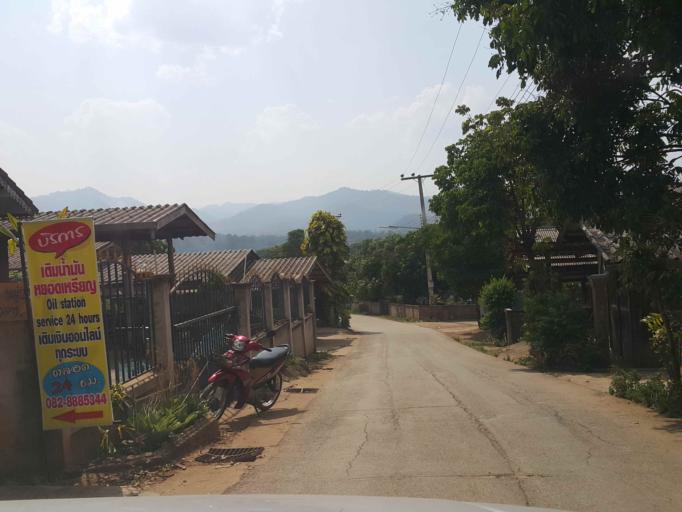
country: TH
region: Chiang Mai
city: Wiang Haeng
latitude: 19.3781
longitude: 98.7238
